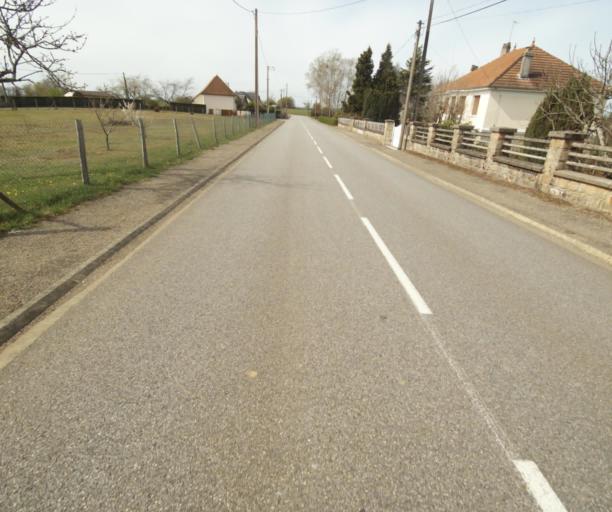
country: FR
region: Limousin
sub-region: Departement de la Correze
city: Correze
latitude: 45.3879
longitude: 1.8110
